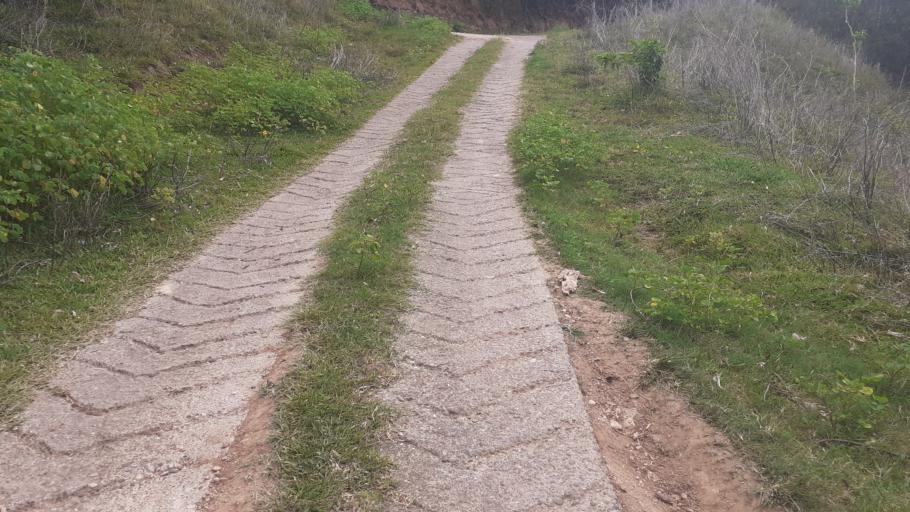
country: VU
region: Tafea
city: Isangel
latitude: -18.8190
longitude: 169.0249
